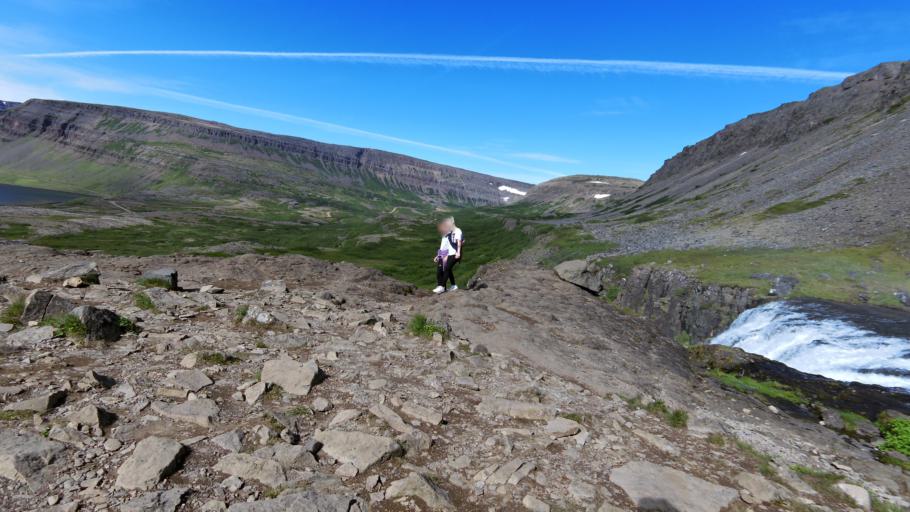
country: IS
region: Westfjords
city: Isafjoerdur
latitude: 65.7328
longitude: -23.2032
